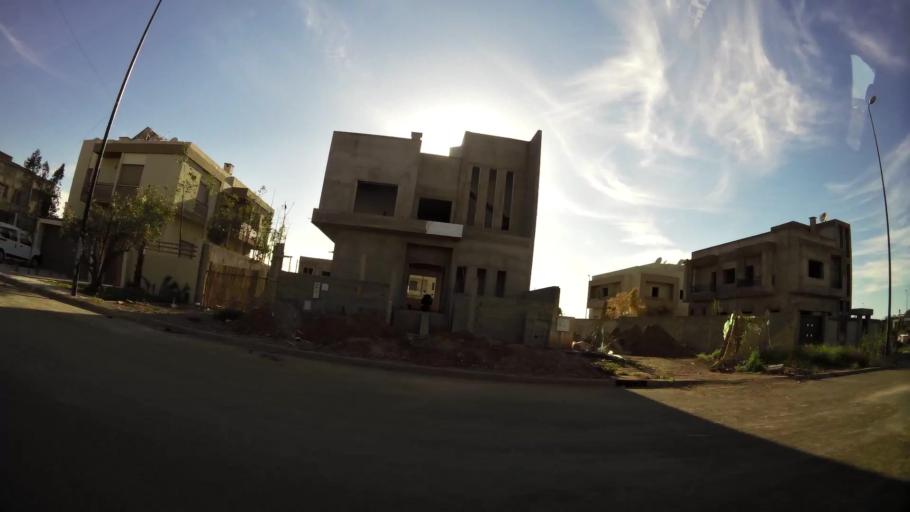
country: MA
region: Marrakech-Tensift-Al Haouz
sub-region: Marrakech
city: Marrakesh
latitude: 31.6727
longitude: -8.0731
